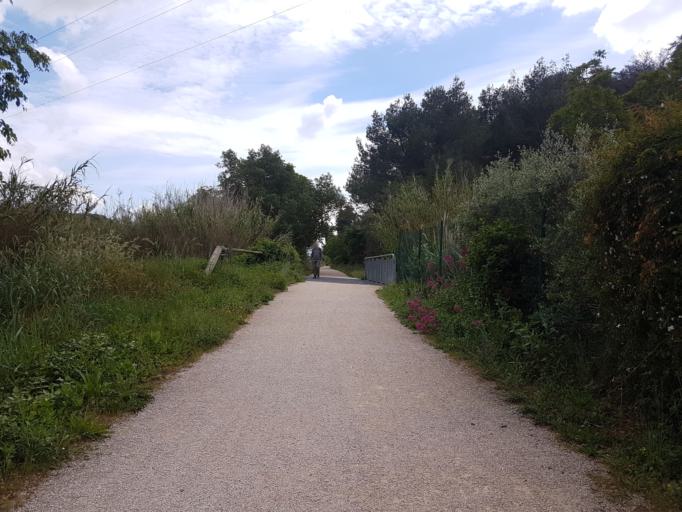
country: FR
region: Languedoc-Roussillon
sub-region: Departement du Gard
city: Beaucaire
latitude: 43.8225
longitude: 4.6279
